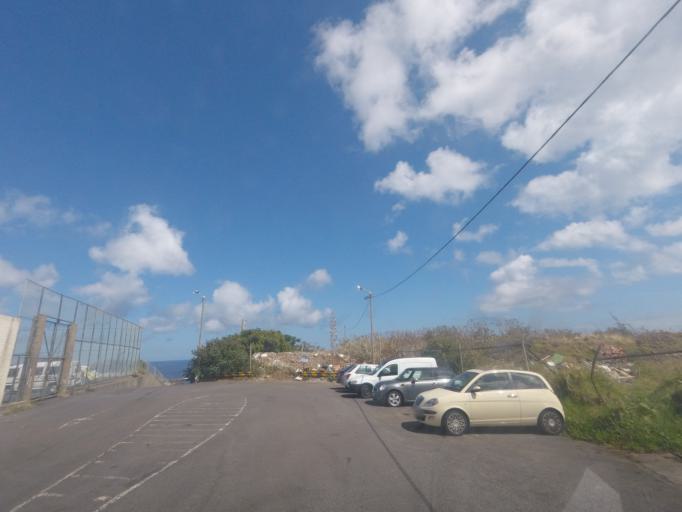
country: PT
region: Madeira
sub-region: Machico
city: Canical
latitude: 32.7366
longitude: -16.7452
